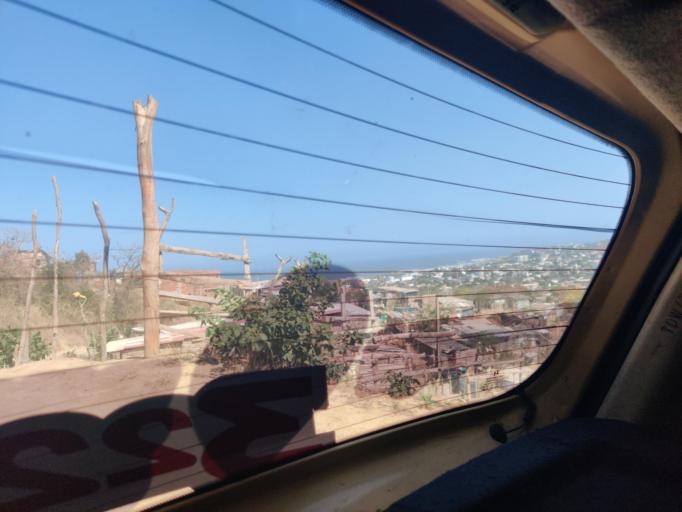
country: CO
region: Atlantico
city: Puerto Colombia
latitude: 10.9791
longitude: -74.9549
